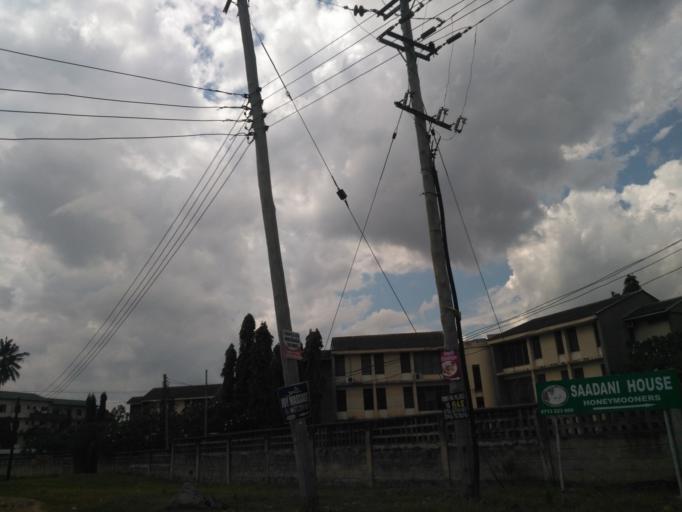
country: TZ
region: Dar es Salaam
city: Magomeni
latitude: -6.7564
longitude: 39.2399
